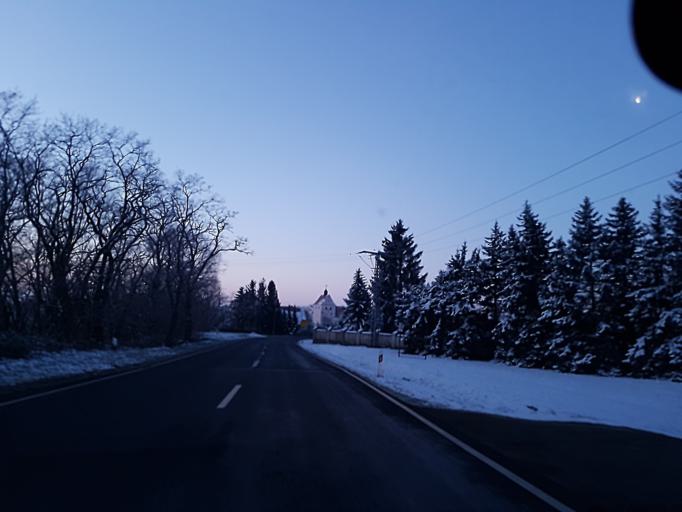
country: DE
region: Brandenburg
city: Muhlberg
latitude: 51.3944
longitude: 13.1870
